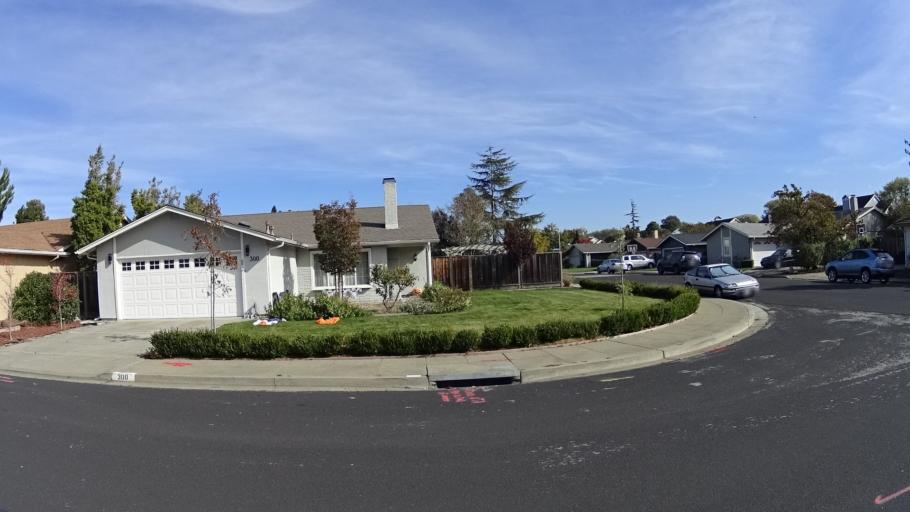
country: US
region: California
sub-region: San Mateo County
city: Belmont
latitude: 37.5365
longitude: -122.2737
